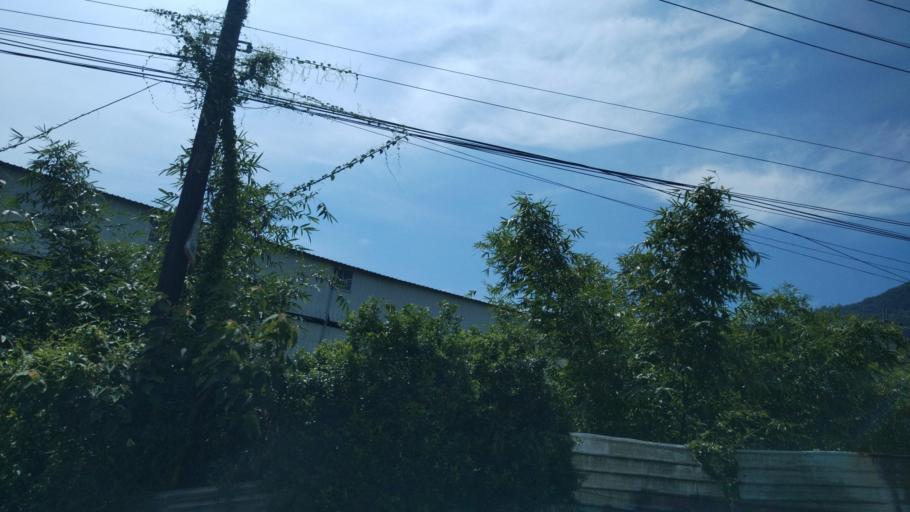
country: TW
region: Taipei
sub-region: Taipei
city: Banqiao
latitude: 24.9512
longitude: 121.5054
